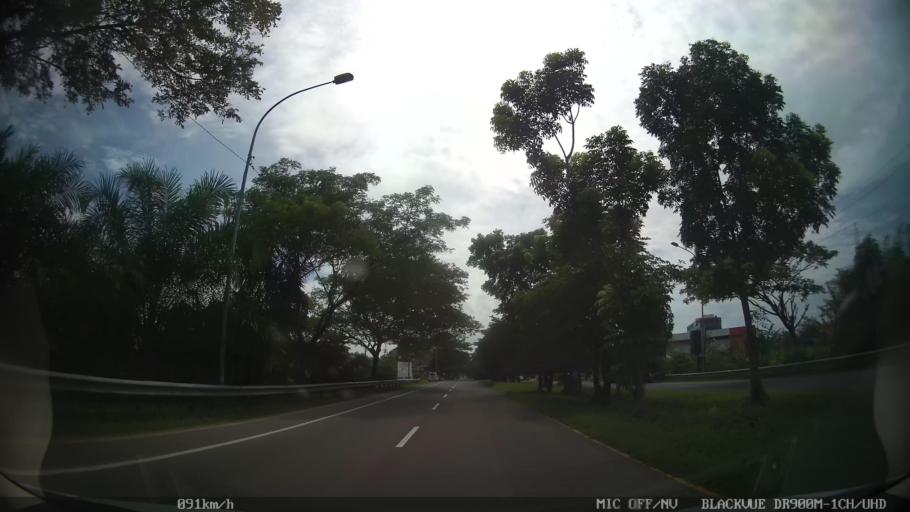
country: ID
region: North Sumatra
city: Percut
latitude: 3.5991
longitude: 98.8281
